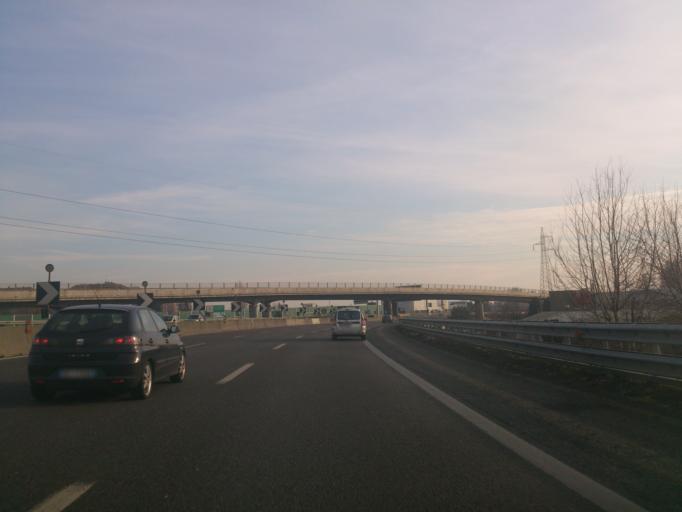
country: IT
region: Lombardy
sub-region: Citta metropolitana di Milano
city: San Donato Milanese
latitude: 45.4085
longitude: 9.2600
